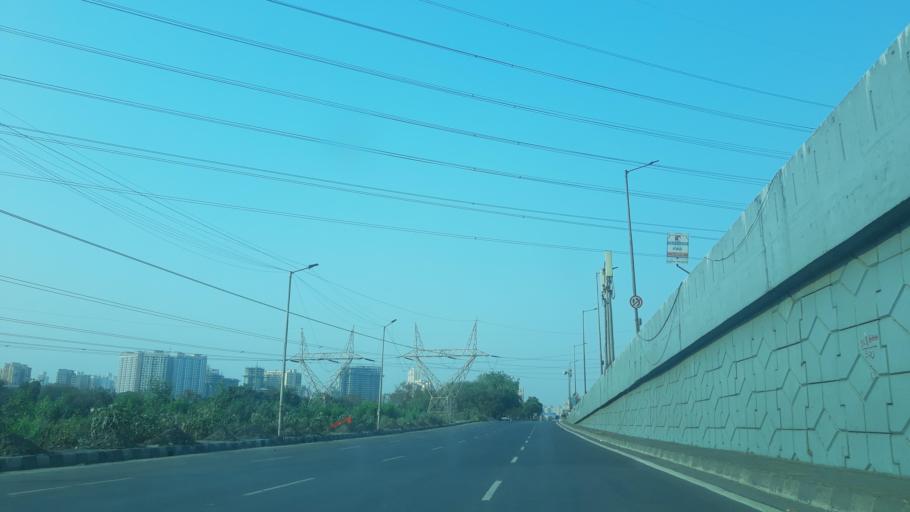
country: IN
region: Maharashtra
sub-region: Thane
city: Airoli
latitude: 19.1562
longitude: 72.9578
